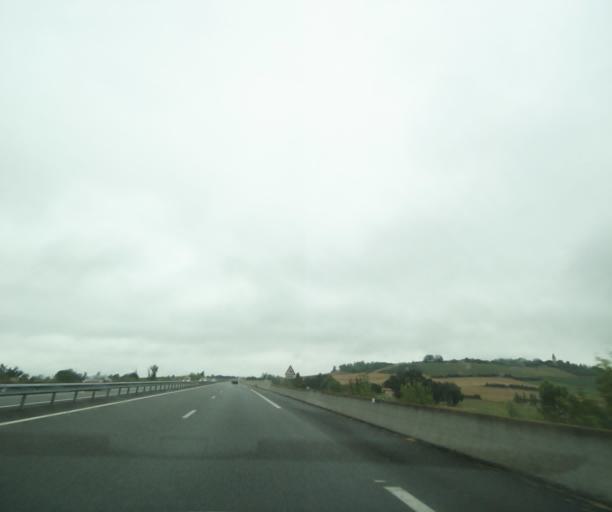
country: FR
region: Midi-Pyrenees
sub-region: Departement du Tarn
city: Le Garric
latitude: 44.0148
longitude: 2.1807
